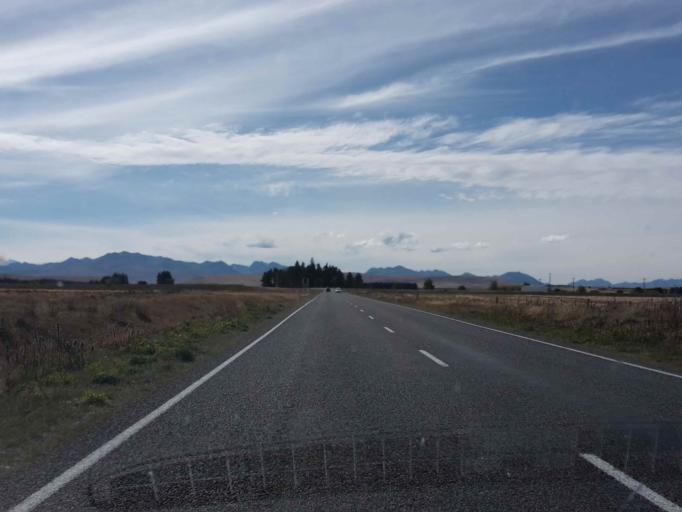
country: NZ
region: Canterbury
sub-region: Timaru District
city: Pleasant Point
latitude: -44.1058
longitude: 170.3535
